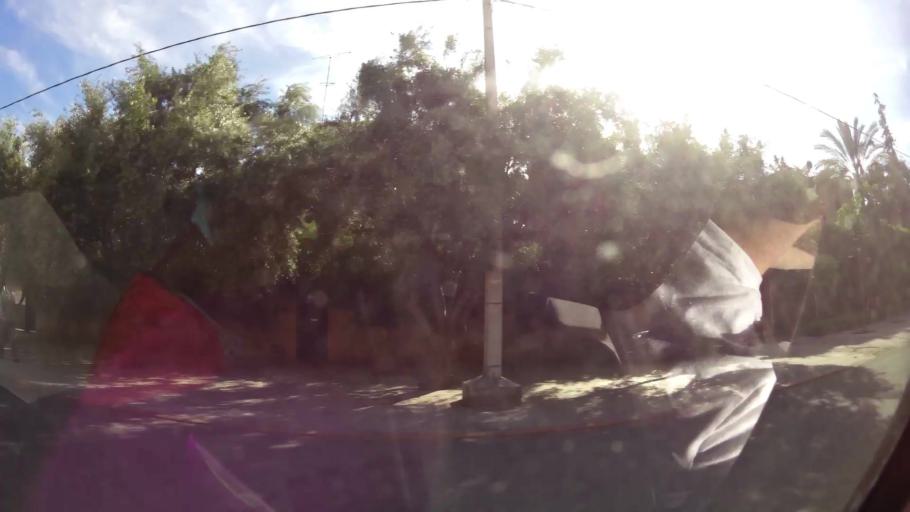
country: MA
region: Marrakech-Tensift-Al Haouz
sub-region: Marrakech
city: Marrakesh
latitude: 31.6523
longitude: -8.0072
